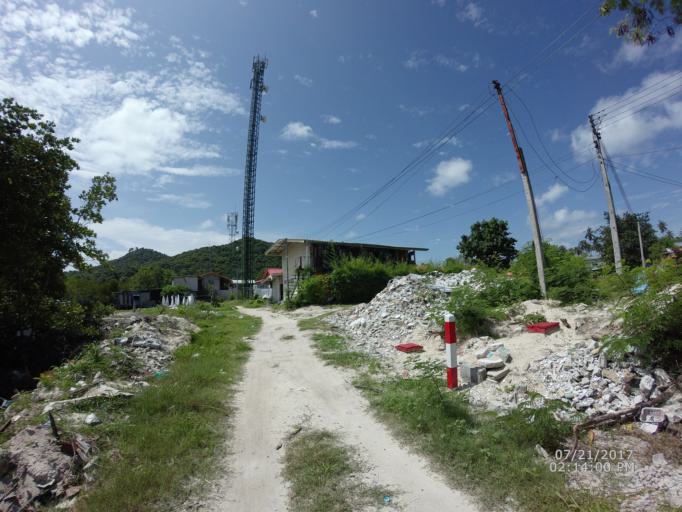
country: TH
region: Phangnga
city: Ban Phru Nai
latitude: 7.7606
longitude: 98.7696
